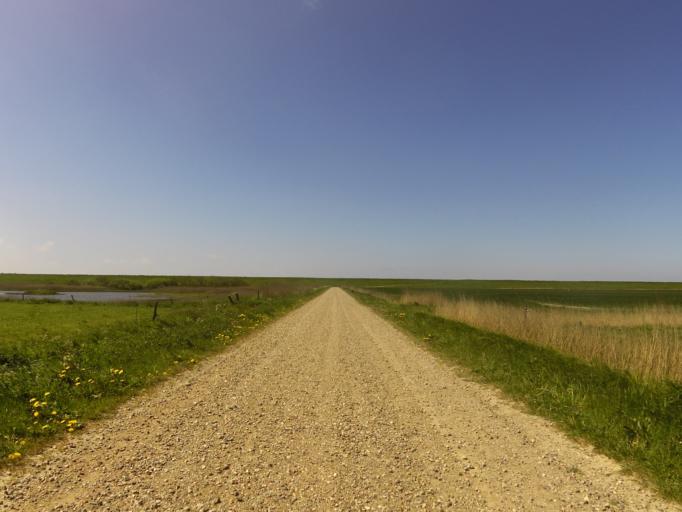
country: DK
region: South Denmark
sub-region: Tonder Kommune
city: Sherrebek
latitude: 55.2361
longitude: 8.6749
